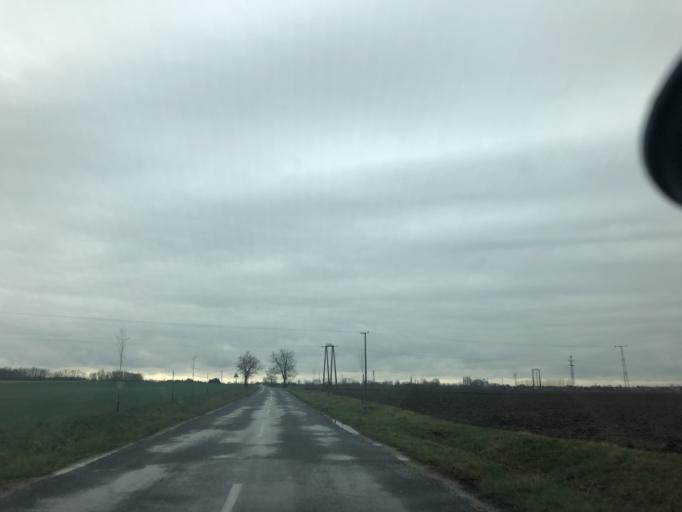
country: HU
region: Gyor-Moson-Sopron
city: Fertoszentmiklos
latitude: 47.6052
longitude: 16.9310
